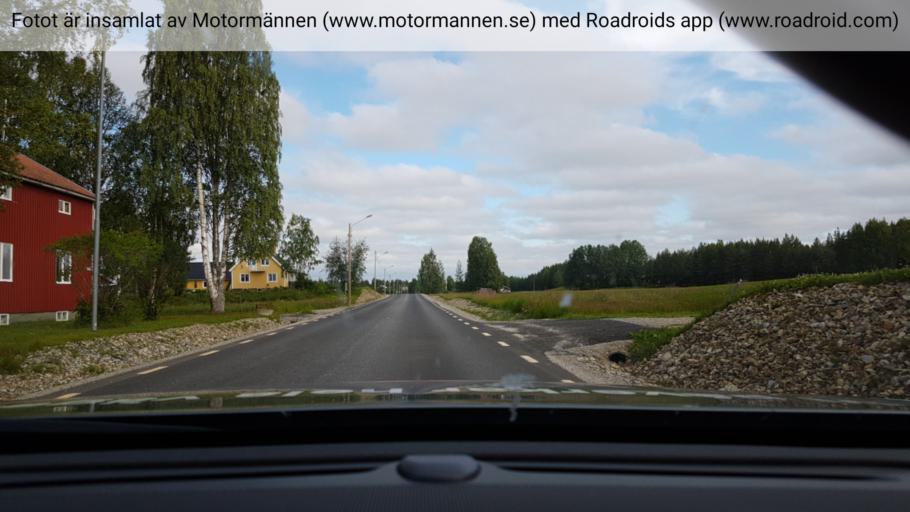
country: SE
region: Vaesterbotten
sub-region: Norsjo Kommun
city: Norsjoe
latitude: 64.5372
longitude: 19.3404
